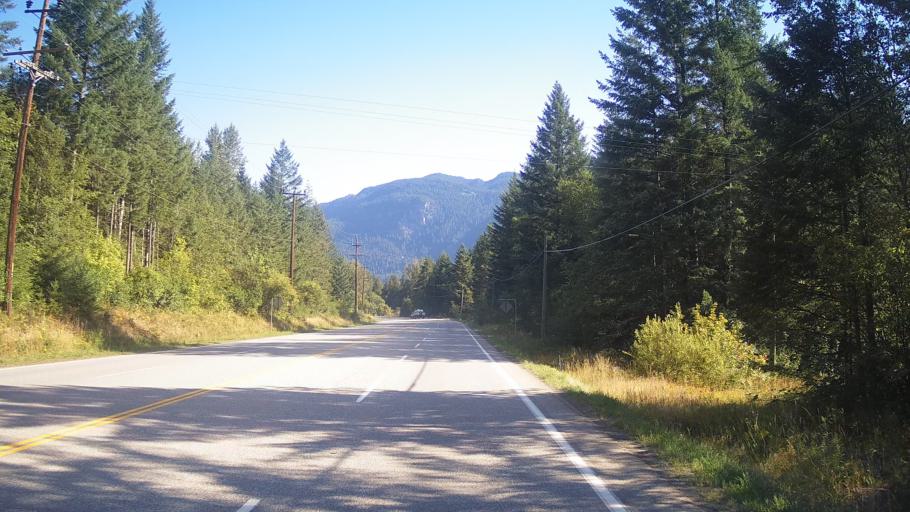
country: CA
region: British Columbia
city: Hope
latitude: 49.6694
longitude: -121.4193
